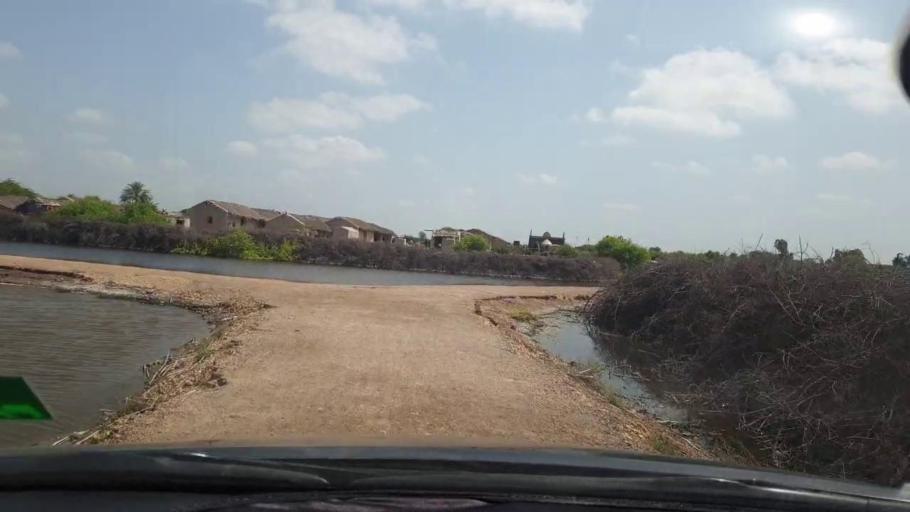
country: PK
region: Sindh
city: Tando Bago
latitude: 24.8561
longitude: 69.0659
